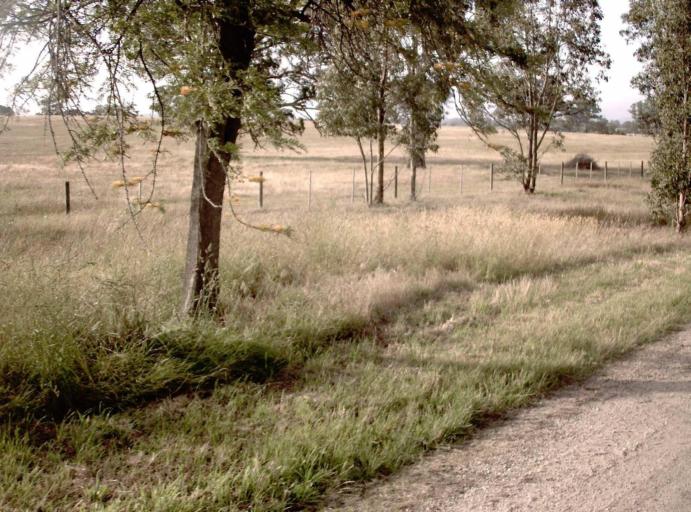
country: AU
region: Victoria
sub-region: Wellington
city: Sale
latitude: -37.9422
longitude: 146.9896
